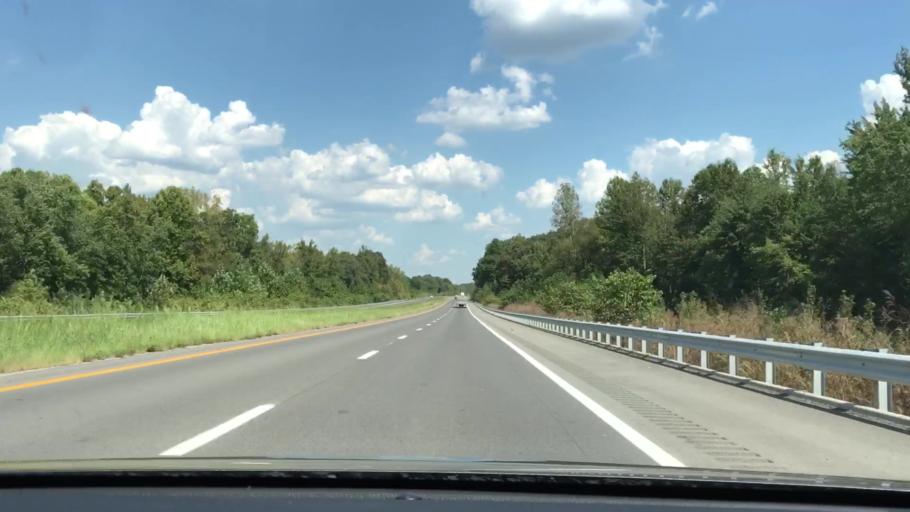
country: US
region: Kentucky
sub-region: Hopkins County
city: Nortonville
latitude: 37.2221
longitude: -87.3865
